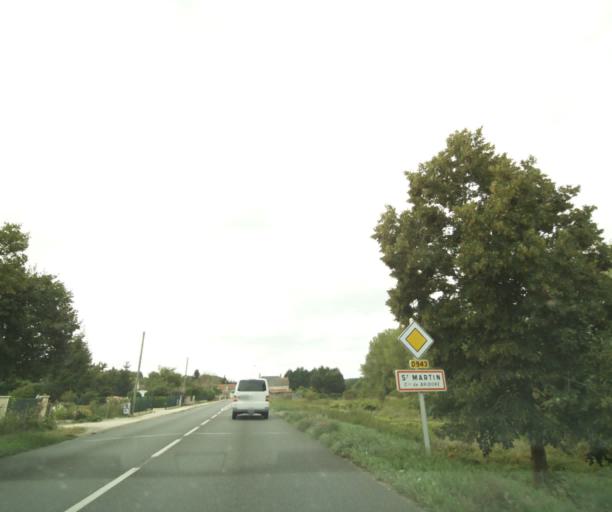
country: FR
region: Centre
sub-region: Departement d'Indre-et-Loire
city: Perrusson
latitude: 47.0574
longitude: 1.0858
